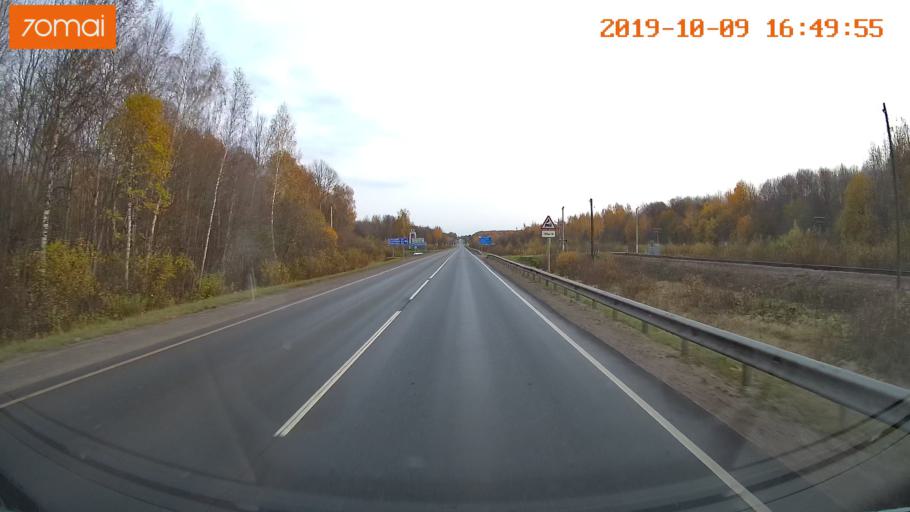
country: RU
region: Kostroma
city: Volgorechensk
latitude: 57.4082
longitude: 41.2021
